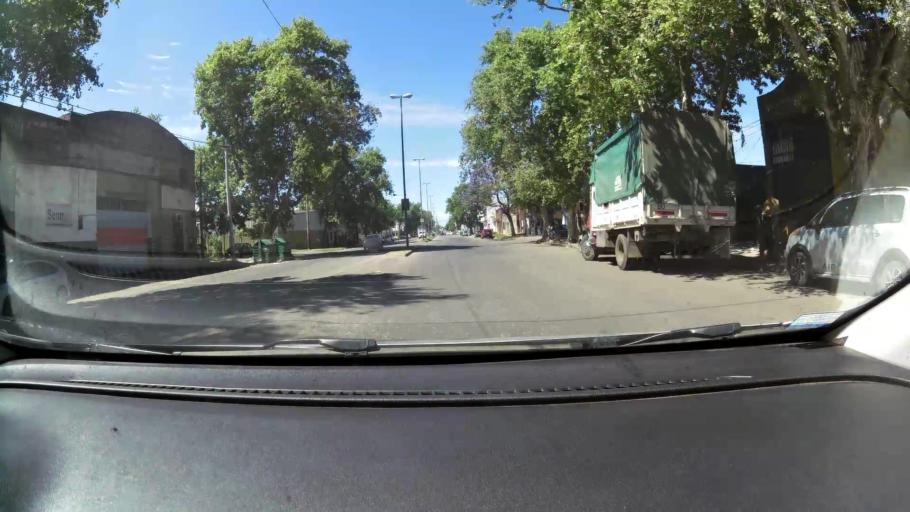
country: AR
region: Santa Fe
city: Perez
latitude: -32.9636
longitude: -60.7117
